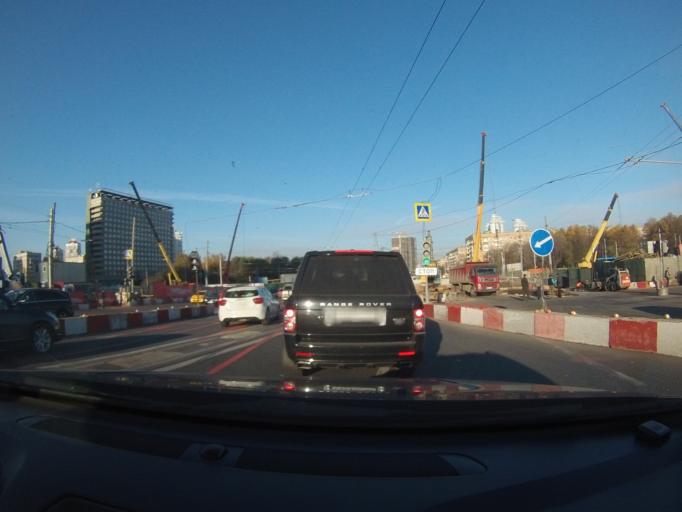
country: RU
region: Moscow
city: Ramenki
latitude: 55.7056
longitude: 37.5148
